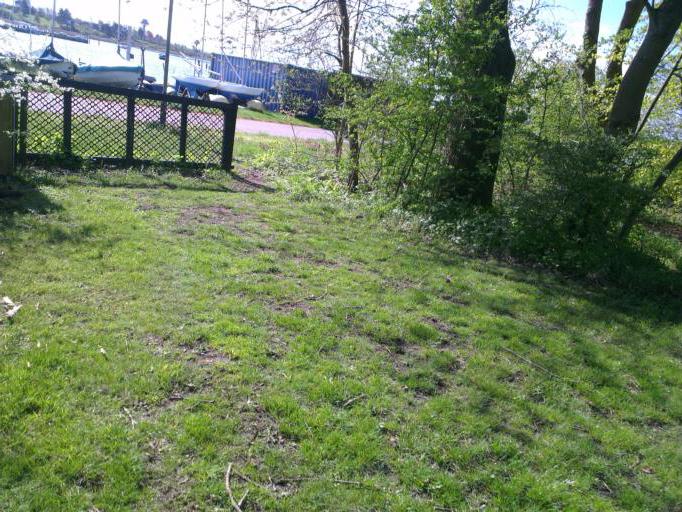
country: DK
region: Capital Region
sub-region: Frederikssund Kommune
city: Frederikssund
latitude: 55.8287
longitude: 12.0583
